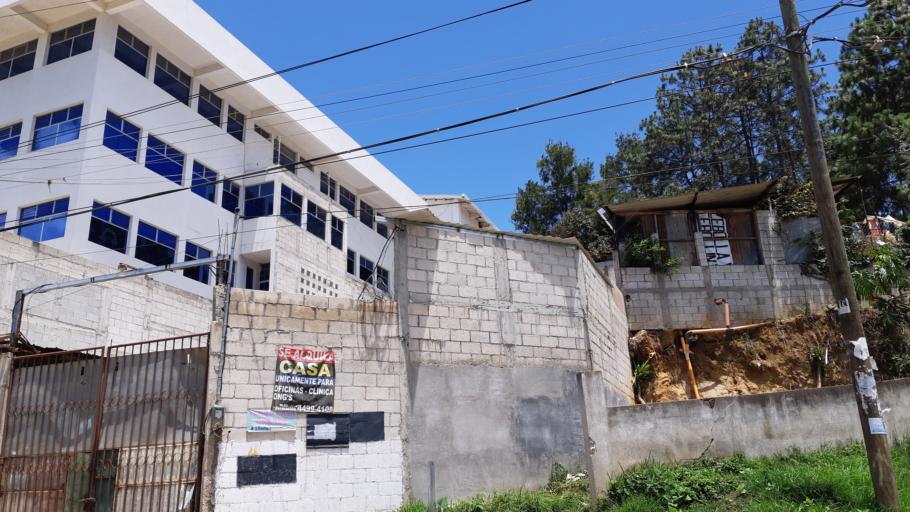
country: GT
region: Chimaltenango
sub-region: Municipio de Chimaltenango
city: Chimaltenango
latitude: 14.6666
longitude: -90.8498
